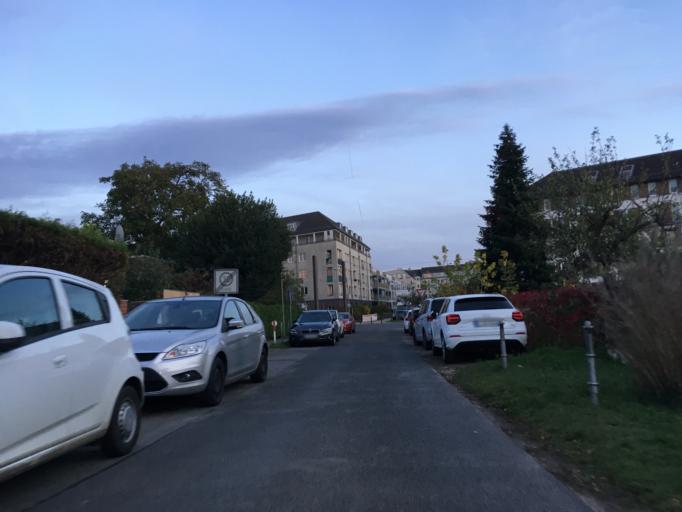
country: DE
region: Berlin
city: Buchholz
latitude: 52.6058
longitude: 13.4164
